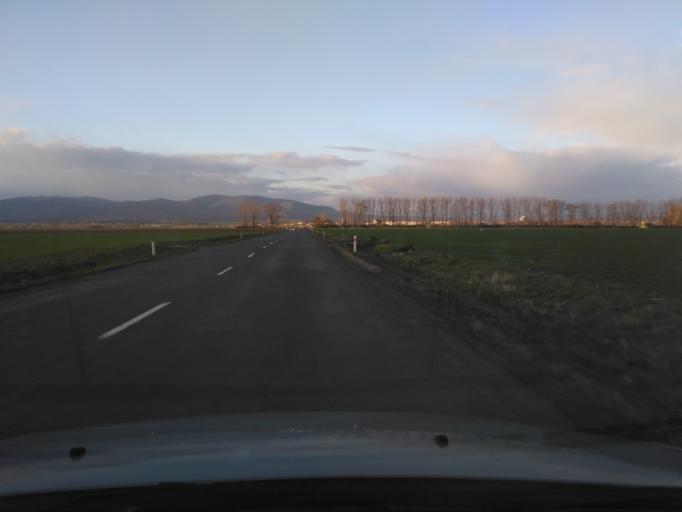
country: SK
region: Kosicky
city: Secovce
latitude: 48.6704
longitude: 21.6605
